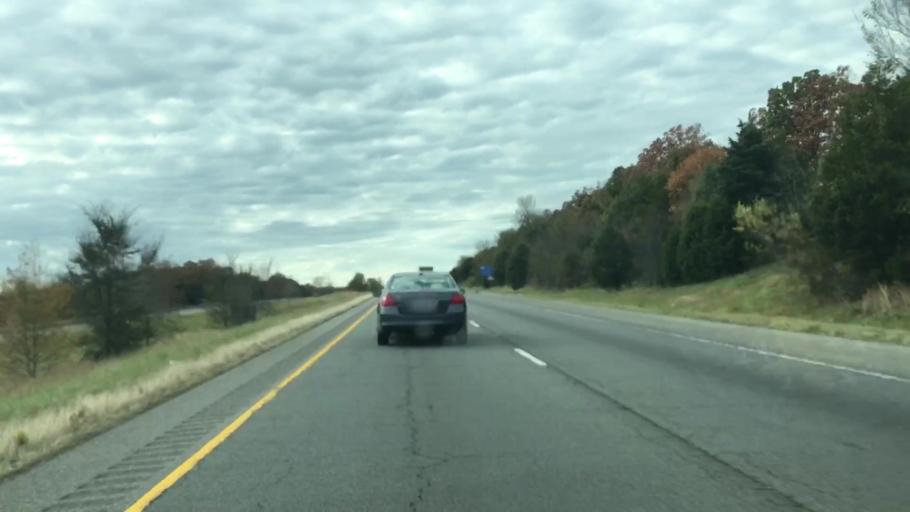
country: US
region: Arkansas
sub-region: Faulkner County
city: Conway
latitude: 35.1222
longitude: -92.4960
